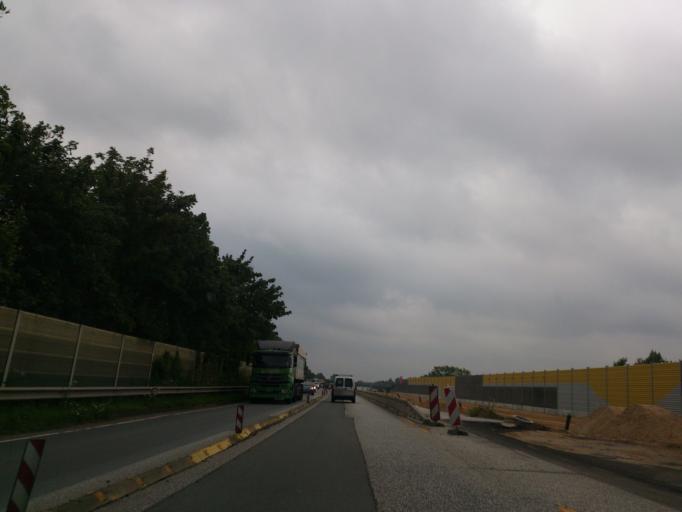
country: DE
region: Schleswig-Holstein
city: Heiligenstedtenerkamp
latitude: 53.9084
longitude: 9.4877
